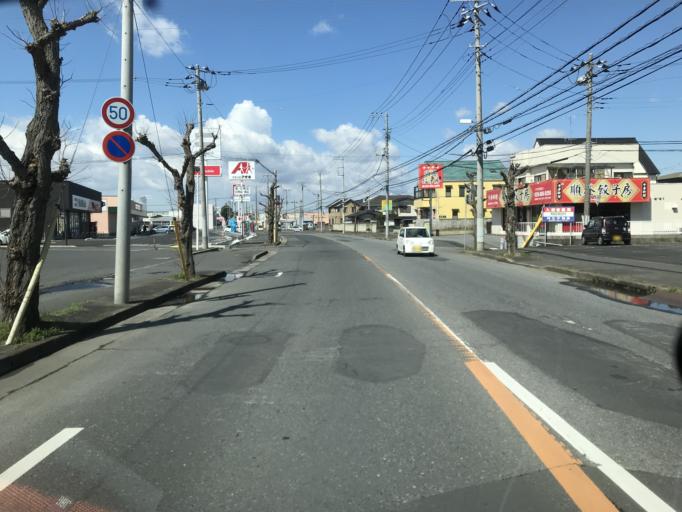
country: JP
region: Ibaraki
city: Ishioka
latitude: 36.1183
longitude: 140.2389
